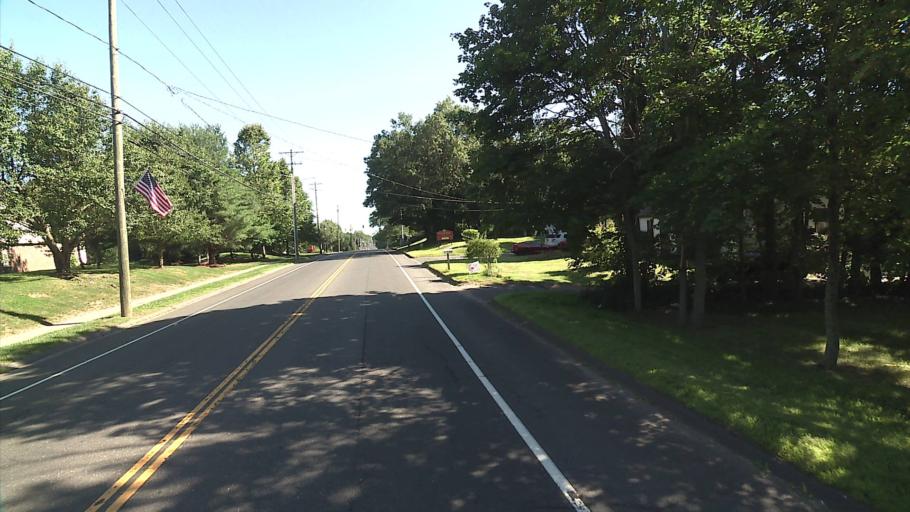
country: US
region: Connecticut
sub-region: New Haven County
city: Cheshire Village
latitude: 41.5058
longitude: -72.9003
